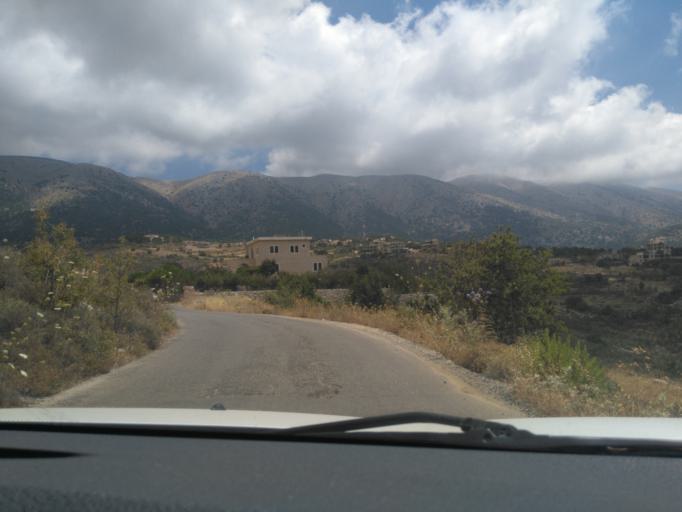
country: LB
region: Mont-Liban
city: Beit ed Dine
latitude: 33.6759
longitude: 35.6634
